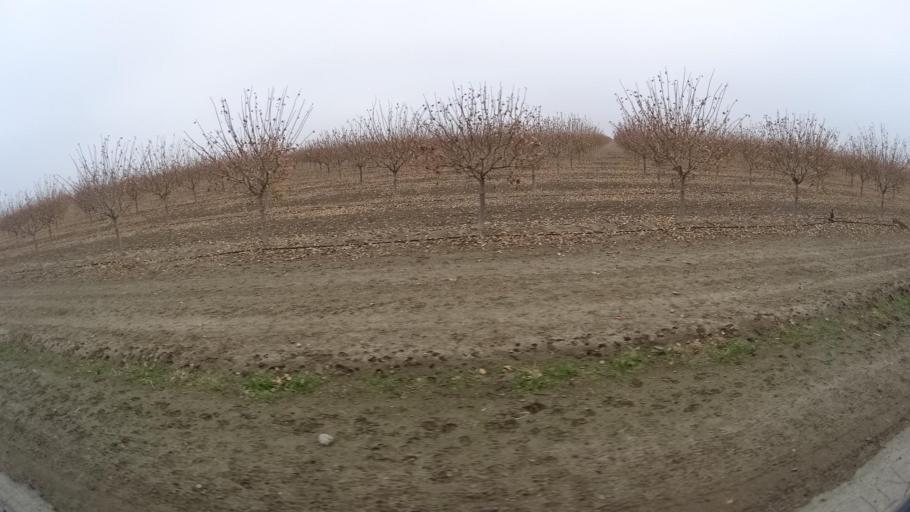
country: US
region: California
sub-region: Kern County
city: Wasco
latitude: 35.6903
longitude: -119.5086
